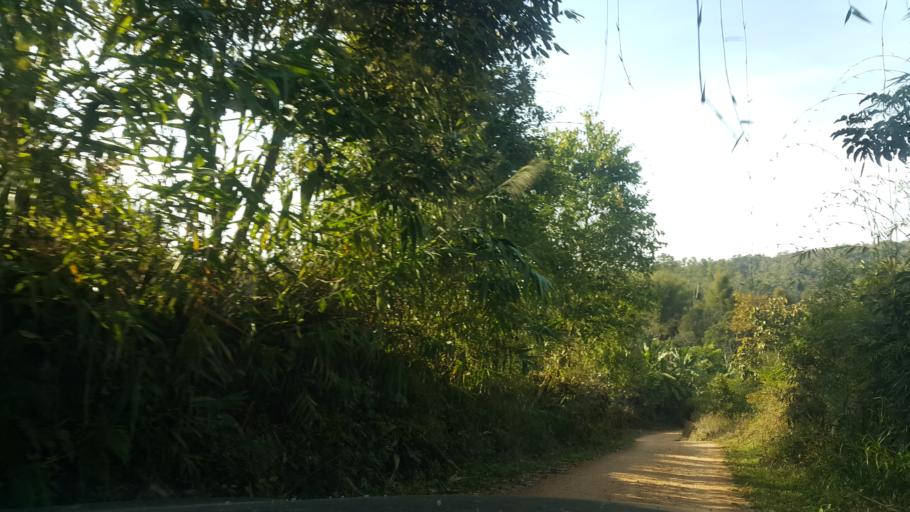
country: TH
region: Chiang Mai
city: Samoeng
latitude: 18.9586
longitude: 98.6732
